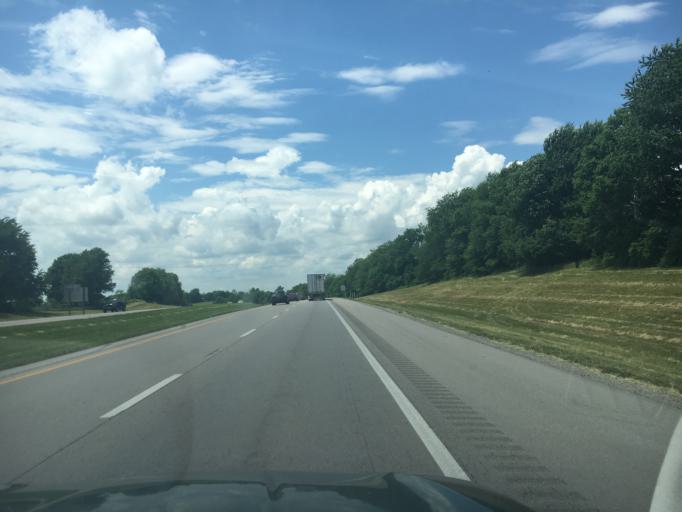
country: US
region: Kentucky
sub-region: Woodford County
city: Midway
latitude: 38.1619
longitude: -84.6233
